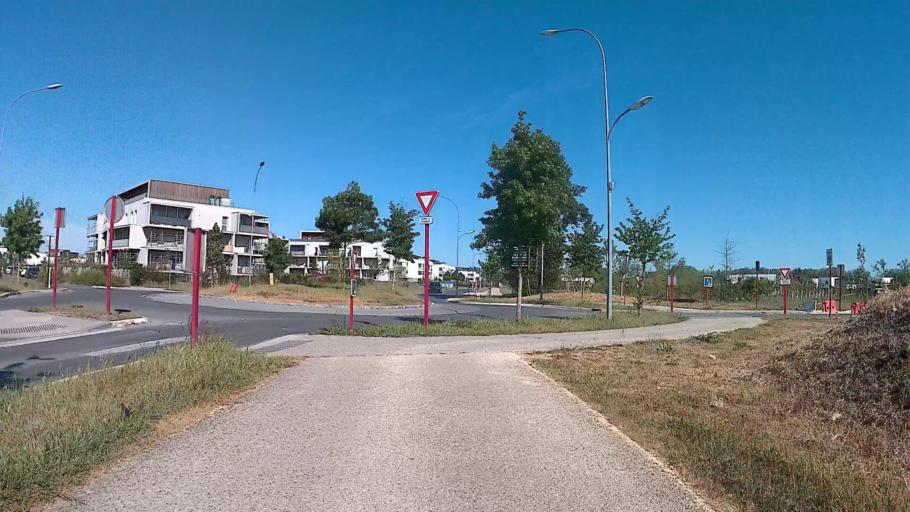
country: FR
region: Aquitaine
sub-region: Departement de la Gironde
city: Villenave-d'Ornon
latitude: 44.7764
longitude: -0.5296
